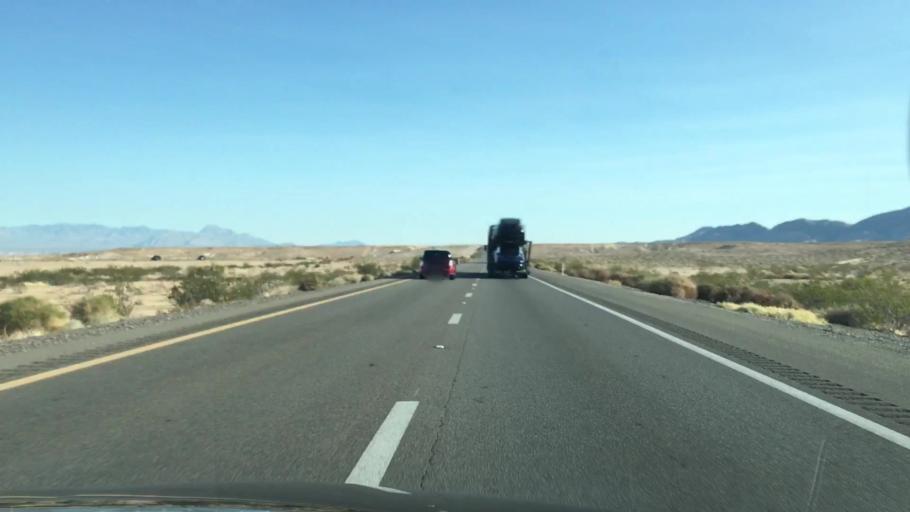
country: US
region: Nevada
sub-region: Clark County
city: Moapa Town
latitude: 36.5623
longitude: -114.6817
